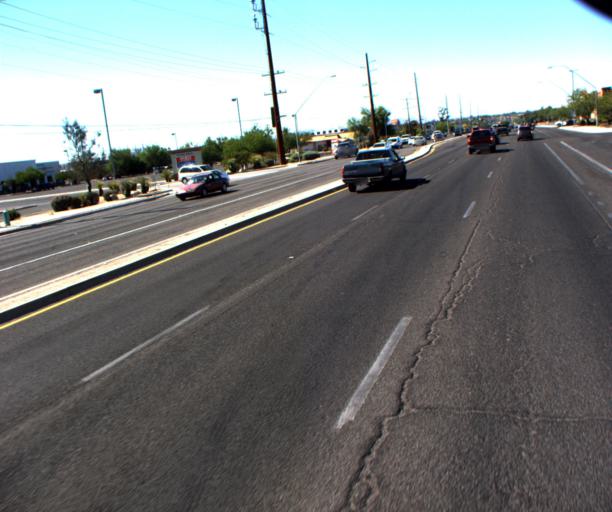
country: US
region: Arizona
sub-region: Pima County
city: Flowing Wells
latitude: 32.2831
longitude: -110.9781
